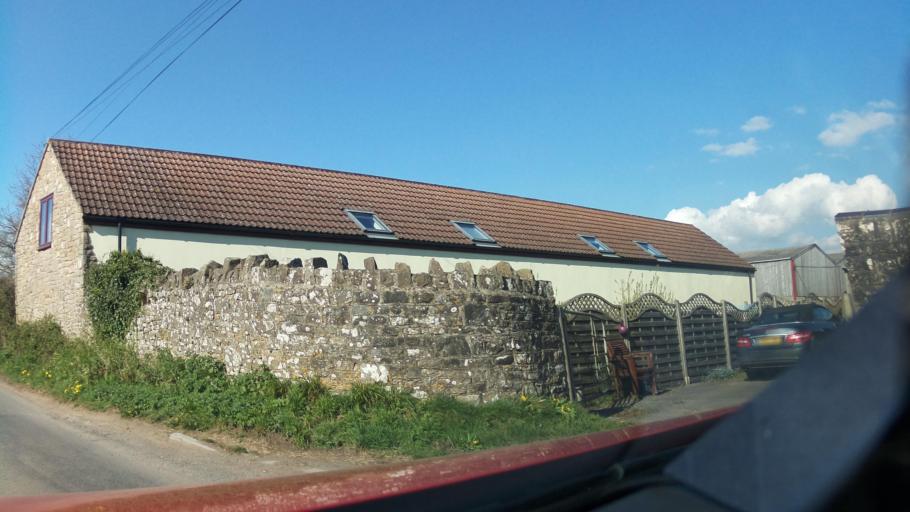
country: GB
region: England
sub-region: South Gloucestershire
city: Alveston
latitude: 51.5967
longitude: -2.5473
